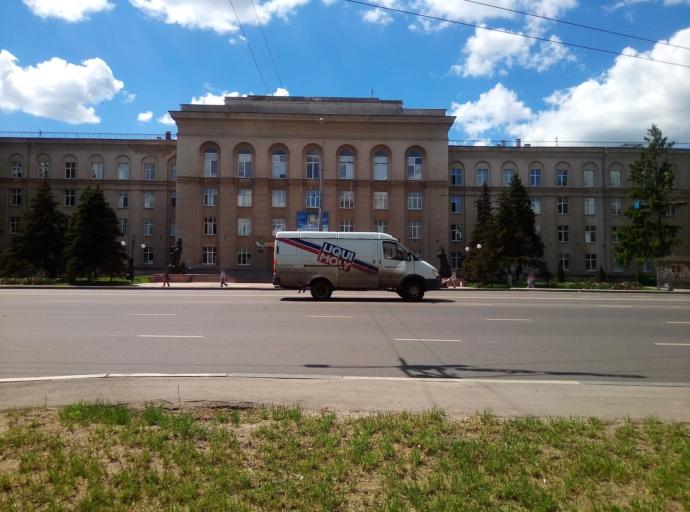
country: RU
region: Kursk
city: Kursk
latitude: 51.7649
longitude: 36.1843
